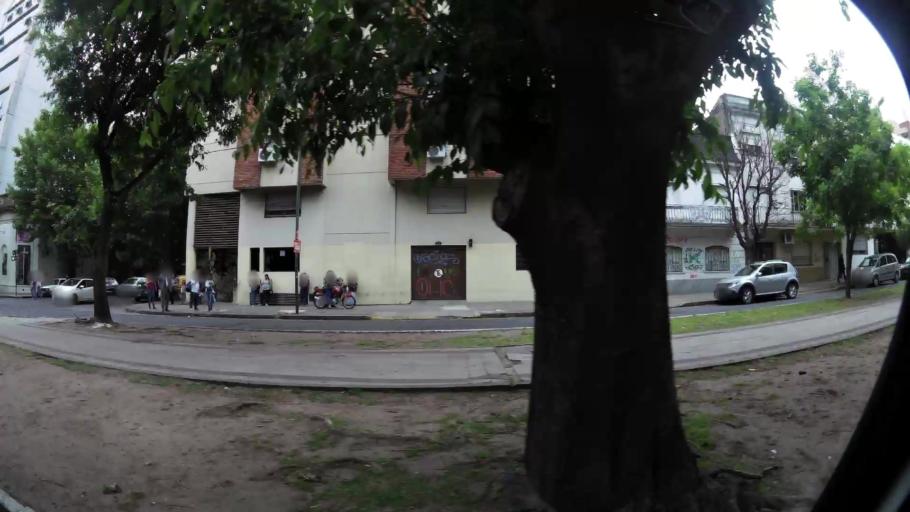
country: AR
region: Buenos Aires
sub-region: Partido de La Plata
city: La Plata
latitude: -34.9244
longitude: -57.9507
